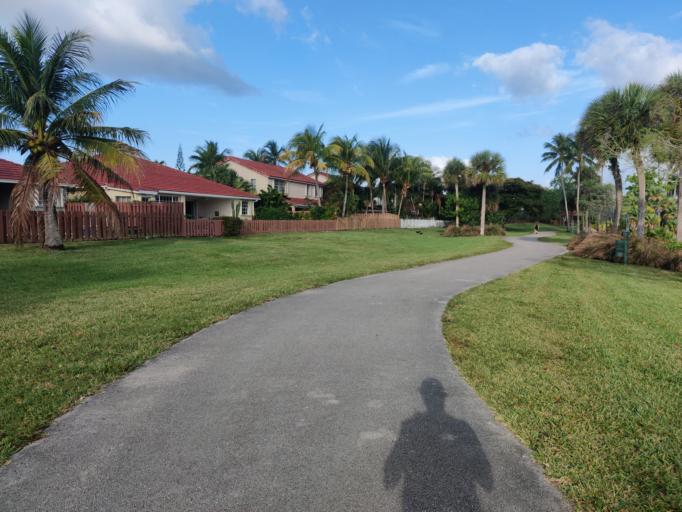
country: US
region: Florida
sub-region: Miami-Dade County
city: The Hammocks
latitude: 25.6662
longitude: -80.4557
